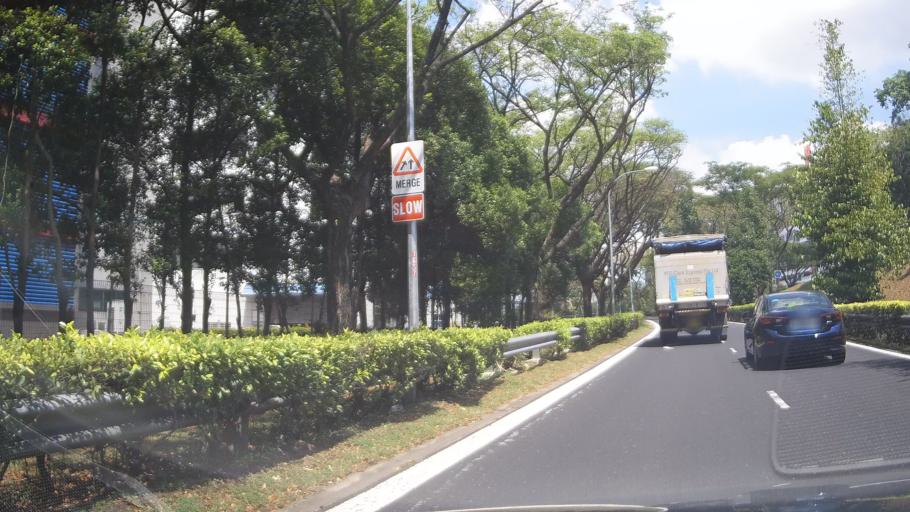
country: SG
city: Singapore
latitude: 1.3354
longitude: 103.7588
